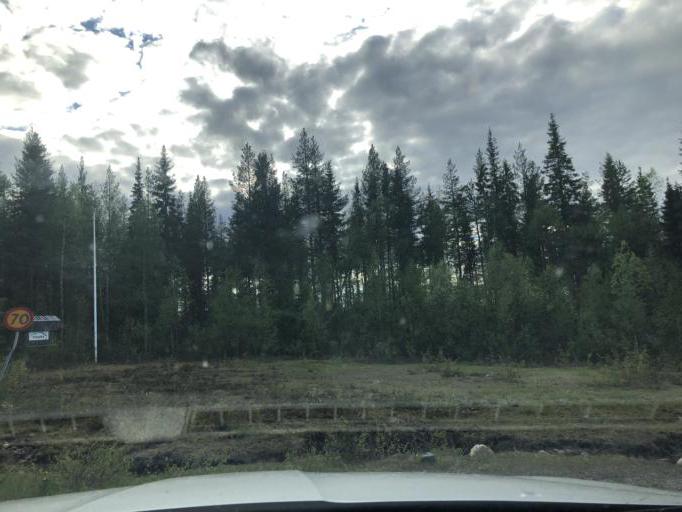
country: SE
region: Norrbotten
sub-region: Arvidsjaurs Kommun
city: Arvidsjaur
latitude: 65.6045
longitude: 19.0982
